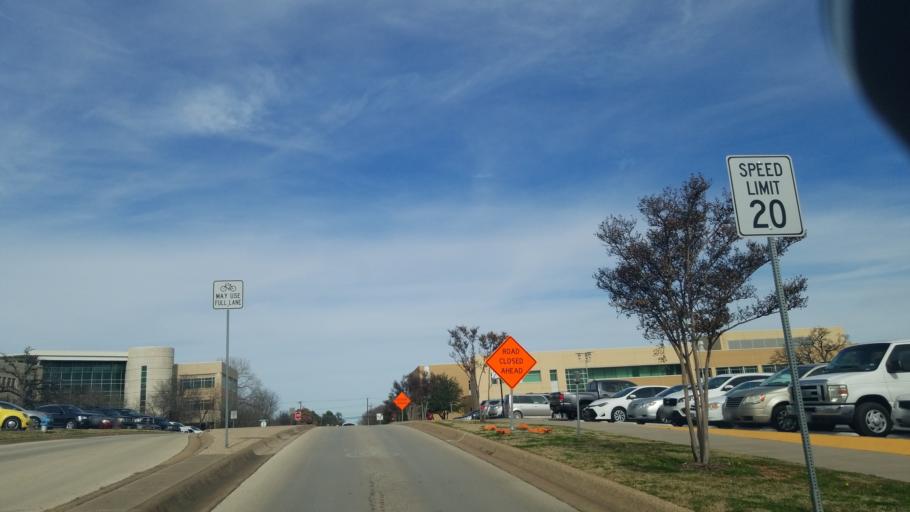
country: US
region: Texas
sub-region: Denton County
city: Denton
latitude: 33.2127
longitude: -97.1506
